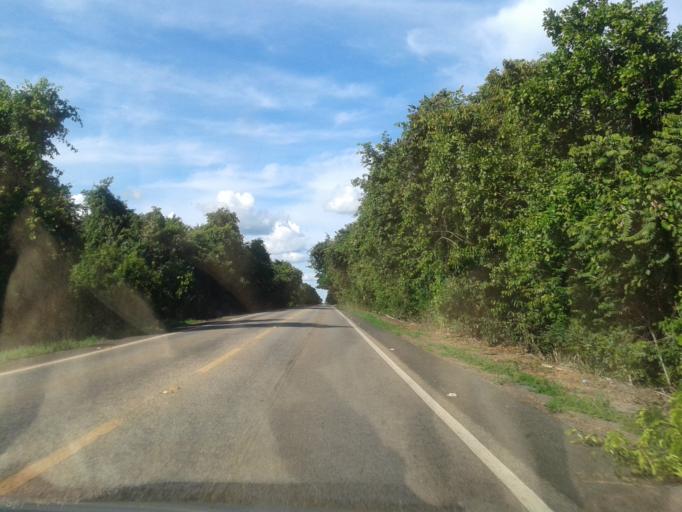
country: BR
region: Goias
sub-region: Mozarlandia
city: Mozarlandia
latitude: -14.6008
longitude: -50.5116
